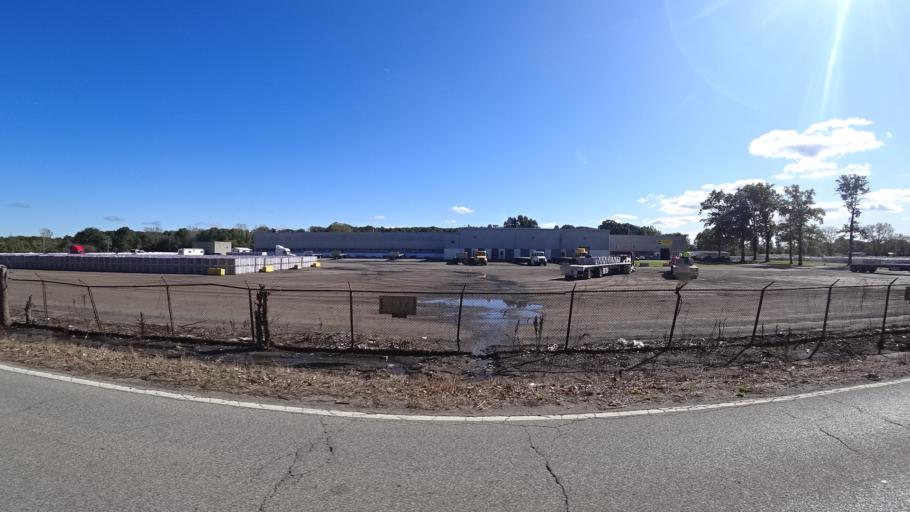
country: US
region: Indiana
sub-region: LaPorte County
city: Michigan City
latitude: 41.6828
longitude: -86.9133
